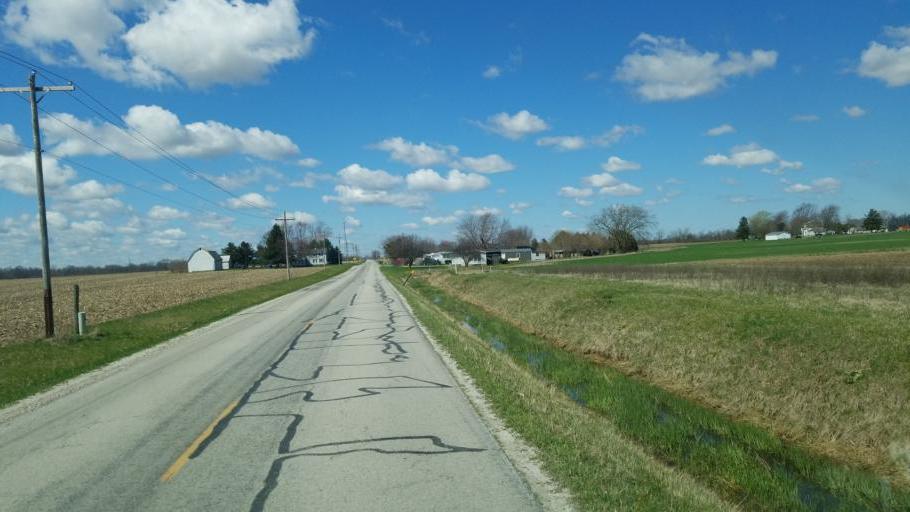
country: US
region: Ohio
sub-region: Sandusky County
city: Green Springs
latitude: 41.2424
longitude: -83.0485
